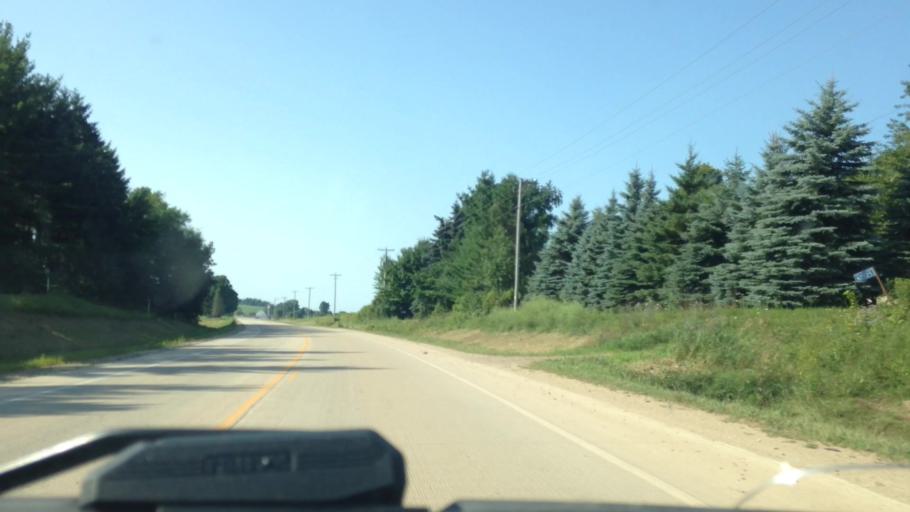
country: US
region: Wisconsin
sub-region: Dodge County
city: Mayville
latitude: 43.4551
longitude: -88.5621
